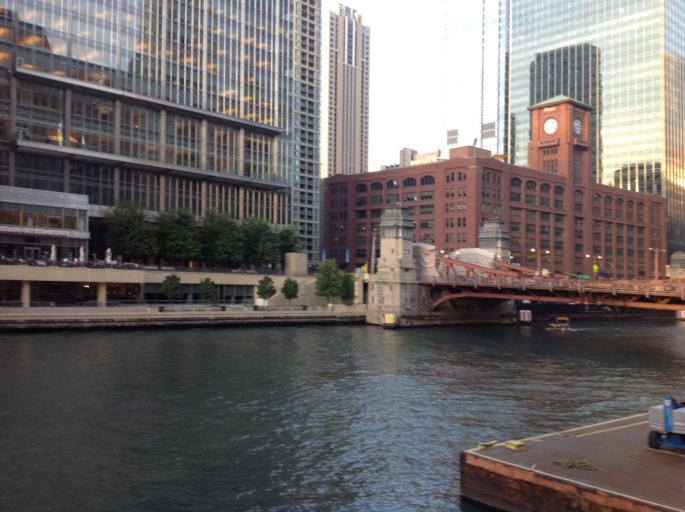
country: US
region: Illinois
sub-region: Cook County
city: Chicago
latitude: 41.8875
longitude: -87.6337
